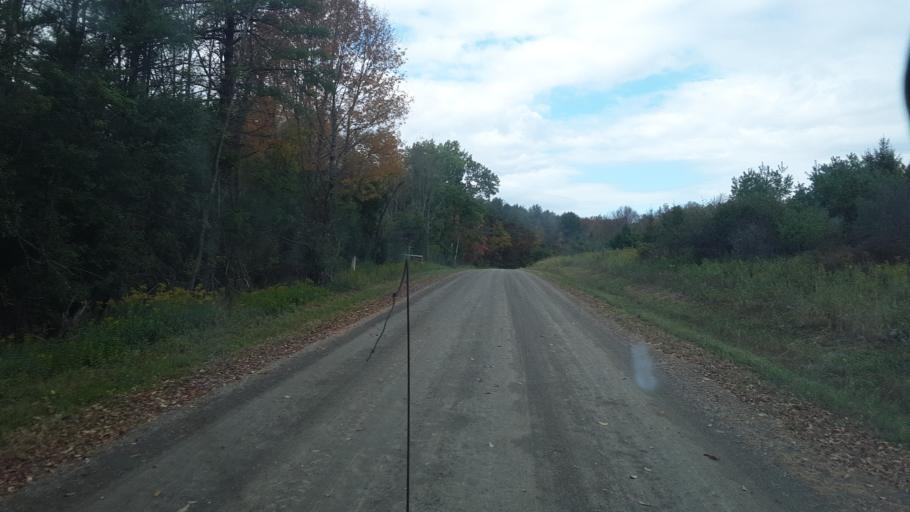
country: US
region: New York
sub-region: Allegany County
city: Alfred
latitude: 42.3869
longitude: -77.8646
